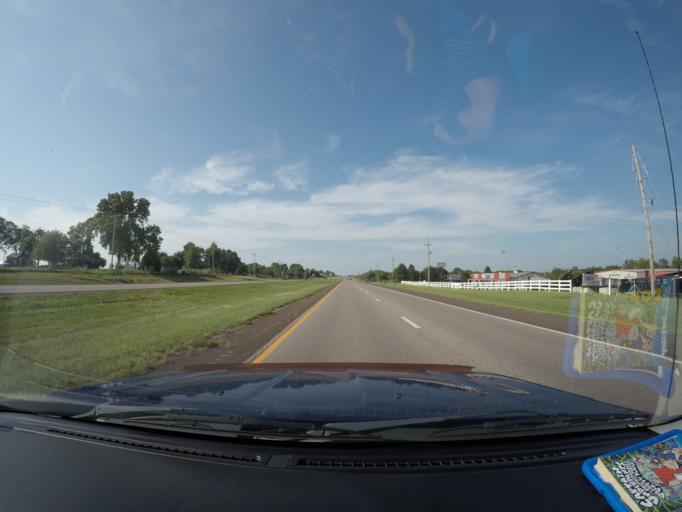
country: US
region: Kansas
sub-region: Leavenworth County
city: Basehor
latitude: 39.1803
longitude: -94.9003
